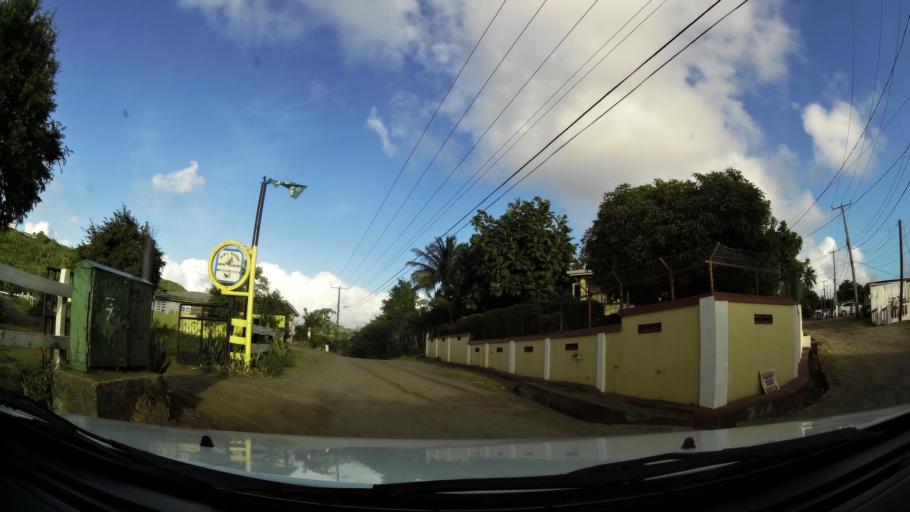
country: LC
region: Gros-Islet
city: Gros Islet
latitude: 14.0816
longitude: -60.9394
